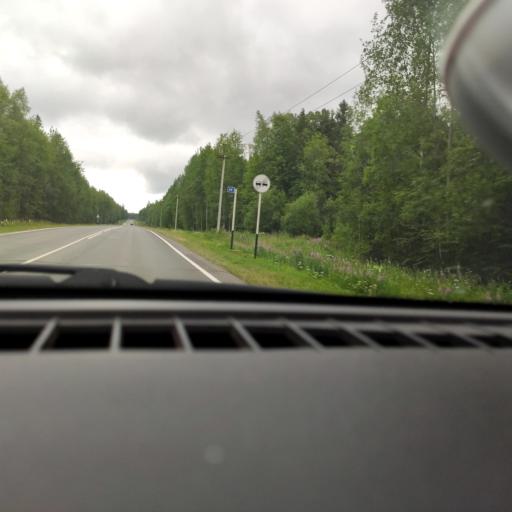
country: RU
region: Perm
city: Polazna
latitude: 58.2980
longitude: 56.1602
